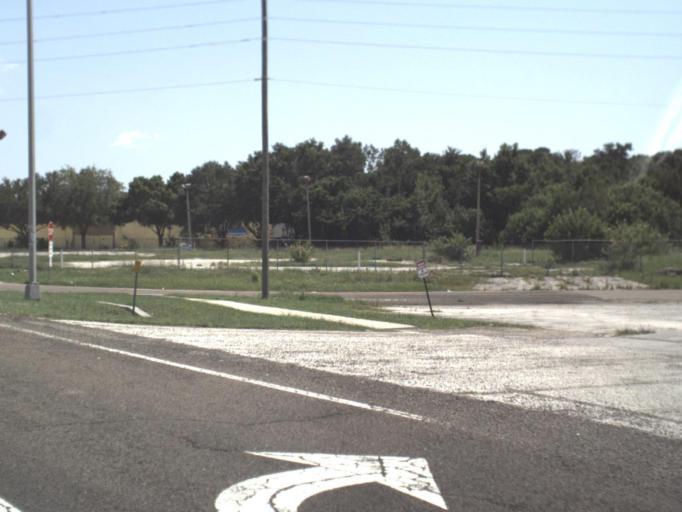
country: US
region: Florida
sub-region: Pinellas County
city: Pinellas Park
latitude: 27.8487
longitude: -82.6907
